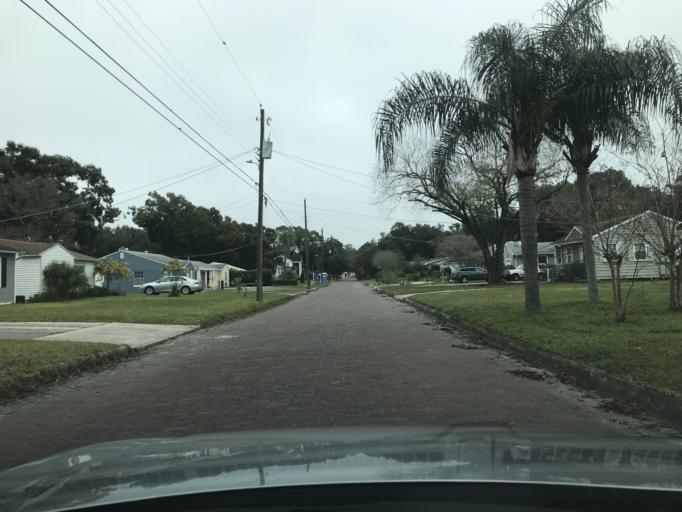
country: US
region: Florida
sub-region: Hillsborough County
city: Tampa
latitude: 27.9780
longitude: -82.4708
